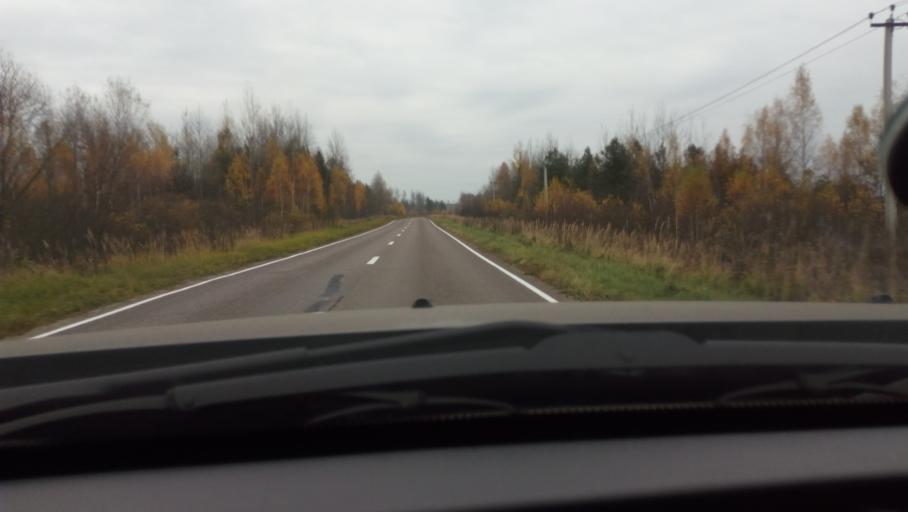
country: RU
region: Moskovskaya
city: Avsyunino
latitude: 55.5941
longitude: 39.2506
